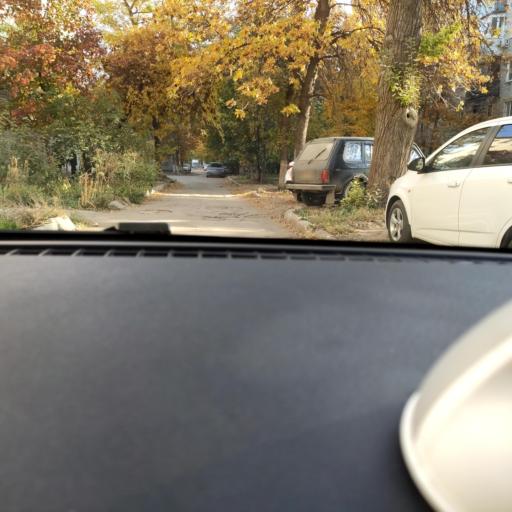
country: RU
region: Samara
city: Petra-Dubrava
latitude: 53.2234
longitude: 50.2724
